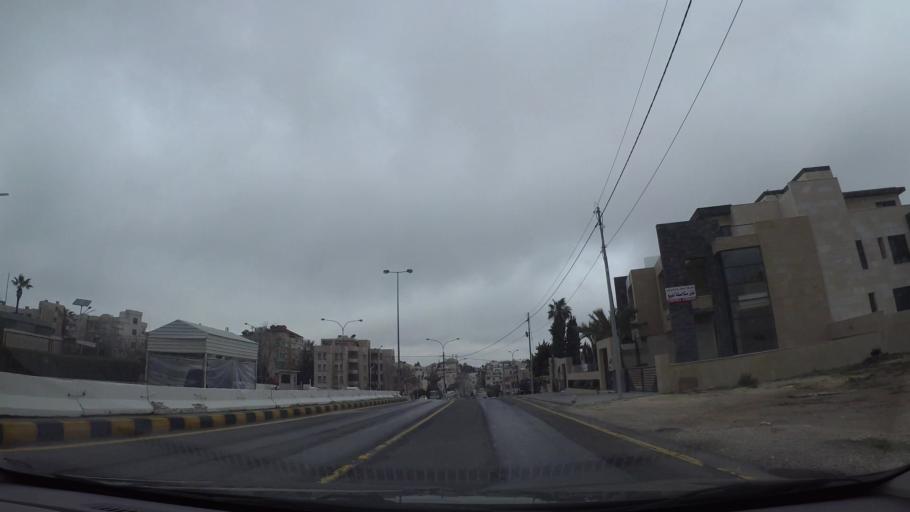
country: JO
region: Amman
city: Al Bunayyat ash Shamaliyah
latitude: 31.9459
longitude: 35.8821
